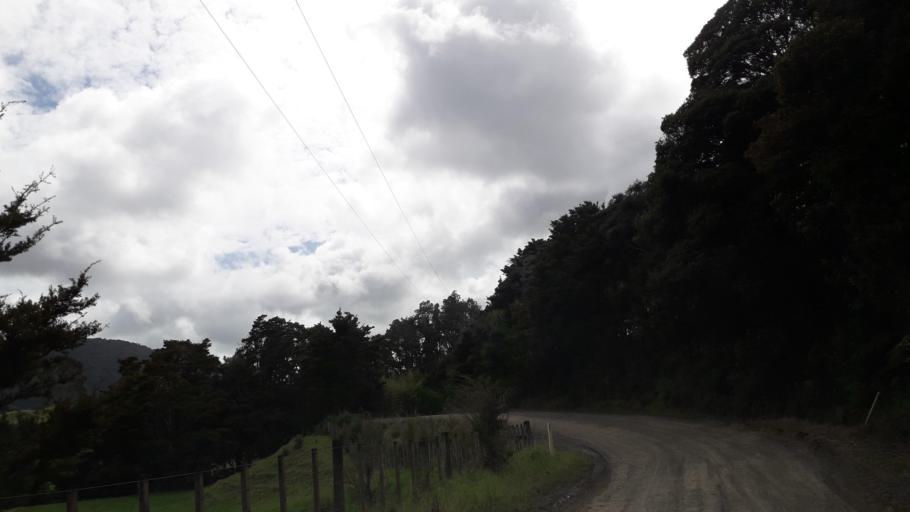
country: NZ
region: Northland
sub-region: Far North District
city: Kaitaia
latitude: -35.2304
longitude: 173.2644
